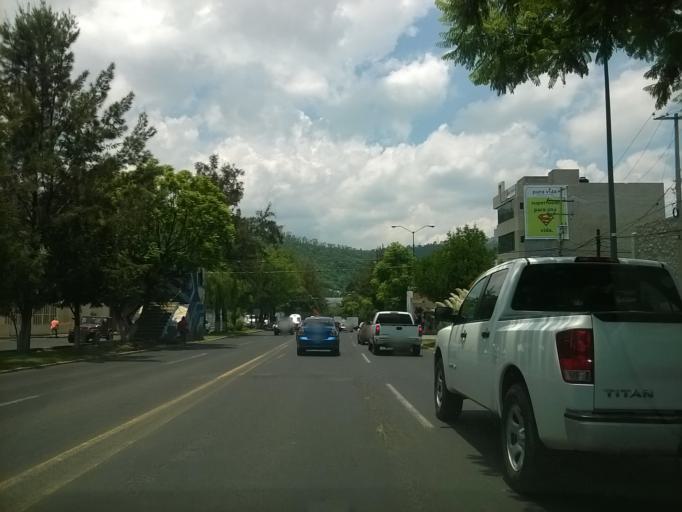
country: MX
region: Michoacan
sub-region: Morelia
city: Puerto de Buenavista (Lazaro Cardenas)
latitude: 19.6919
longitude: -101.1501
